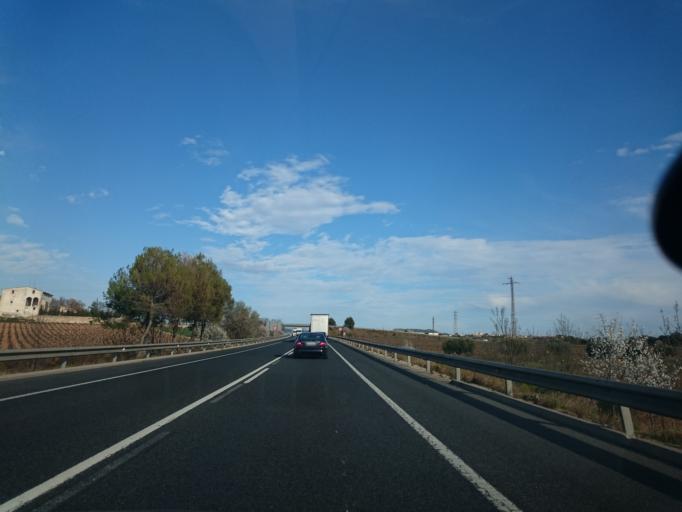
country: ES
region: Catalonia
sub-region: Provincia de Barcelona
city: Vilafranca del Penedes
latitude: 41.3326
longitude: 1.6602
